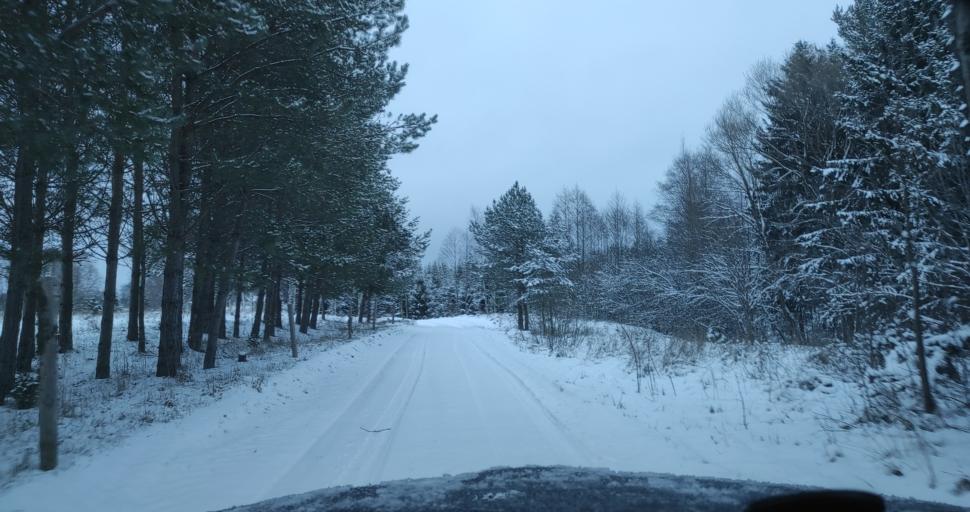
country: LV
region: Alsunga
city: Alsunga
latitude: 56.9561
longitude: 21.6172
